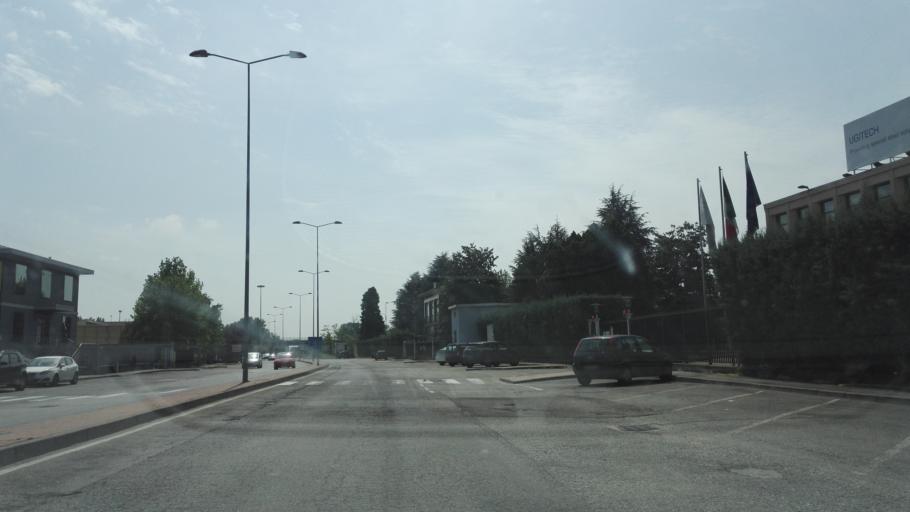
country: IT
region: Lombardy
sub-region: Citta metropolitana di Milano
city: Mezzate
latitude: 45.4266
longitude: 9.2888
